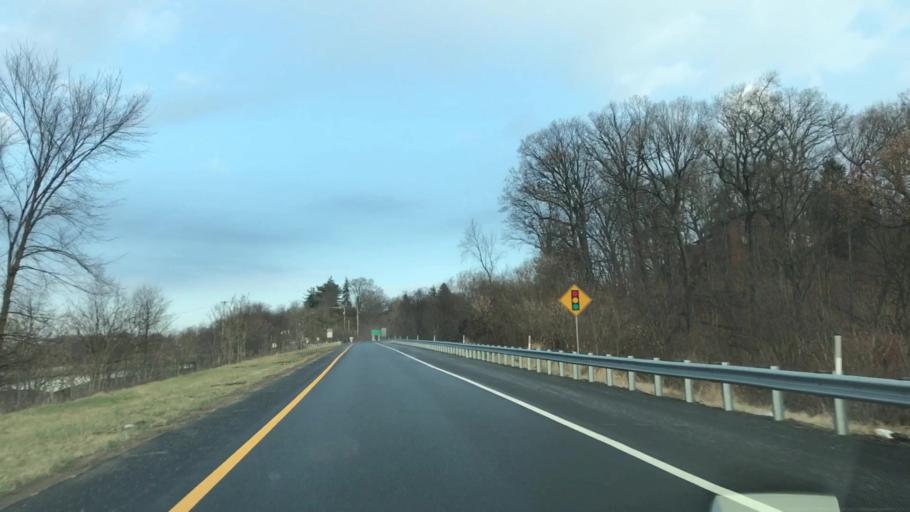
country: US
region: Pennsylvania
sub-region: Allegheny County
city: West View
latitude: 40.5154
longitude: -80.0516
